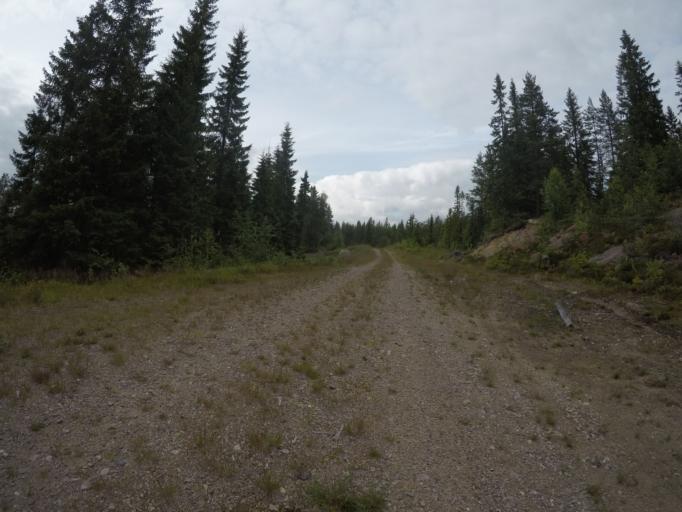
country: SE
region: Vaermland
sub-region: Filipstads Kommun
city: Lesjofors
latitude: 60.2051
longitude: 14.2630
